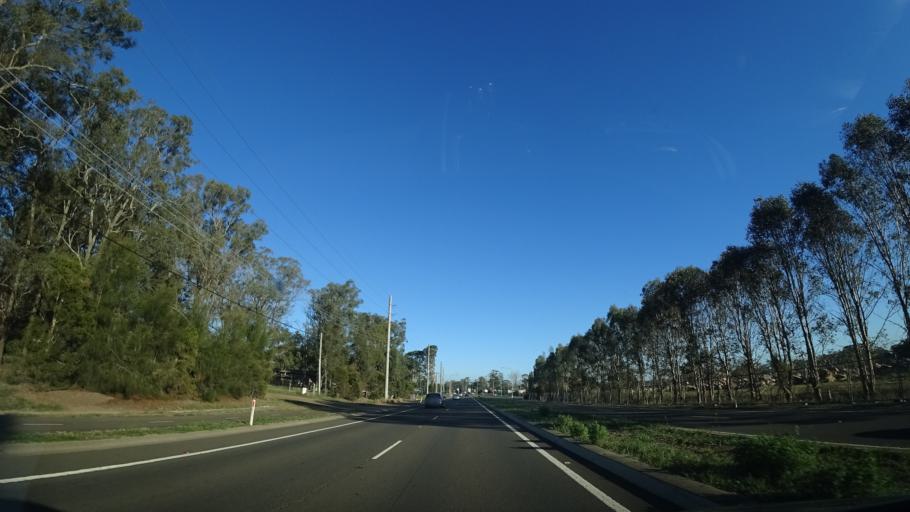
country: AU
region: New South Wales
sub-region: Blacktown
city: Riverstone
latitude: -33.6406
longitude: 150.8524
